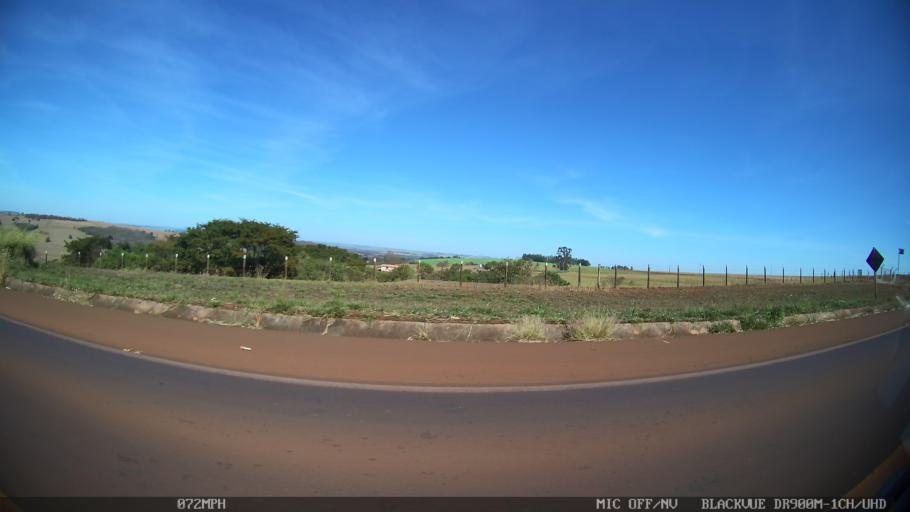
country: BR
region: Sao Paulo
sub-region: Sao Joaquim Da Barra
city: Sao Joaquim da Barra
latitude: -20.5604
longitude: -47.6931
